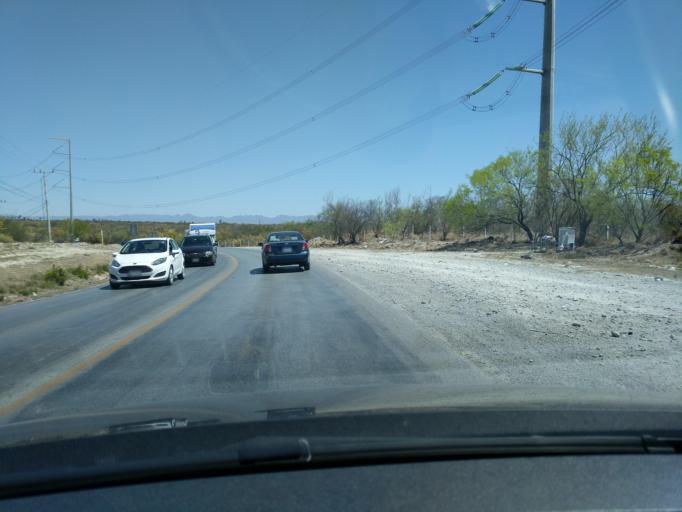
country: MX
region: Nuevo Leon
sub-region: Apodaca
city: Artemio Trevino
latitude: 25.8186
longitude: -100.1458
